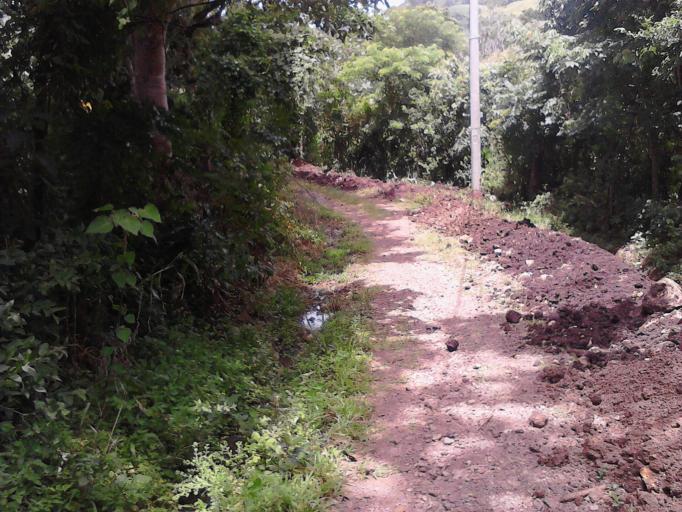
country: NI
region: Matagalpa
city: Matagalpa
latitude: 12.8690
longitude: -85.9183
